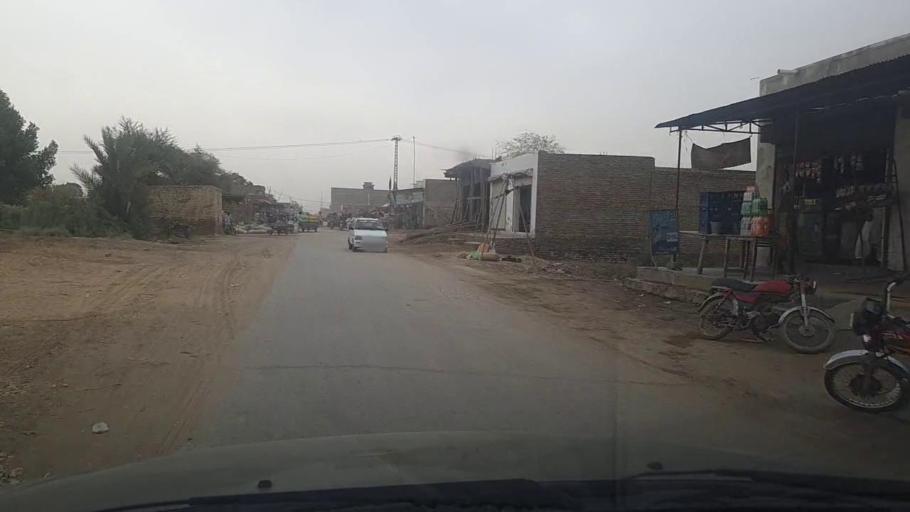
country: PK
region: Sindh
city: Daur
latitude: 26.4572
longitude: 68.3053
